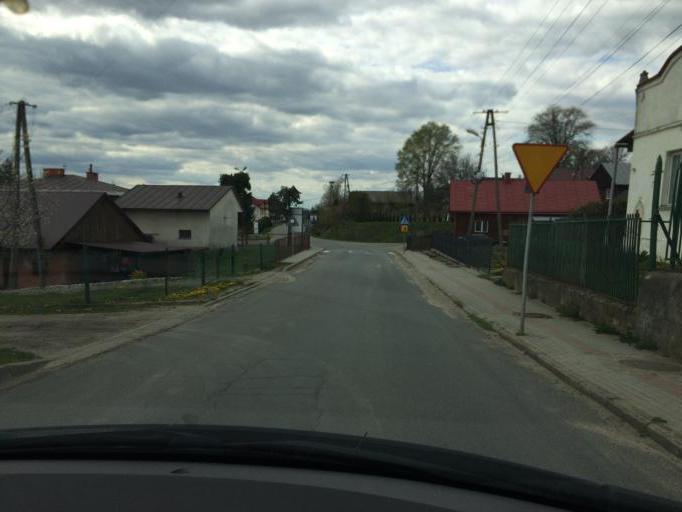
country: PL
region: Subcarpathian Voivodeship
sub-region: Powiat krosnienski
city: Chorkowka
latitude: 49.6074
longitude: 21.6455
